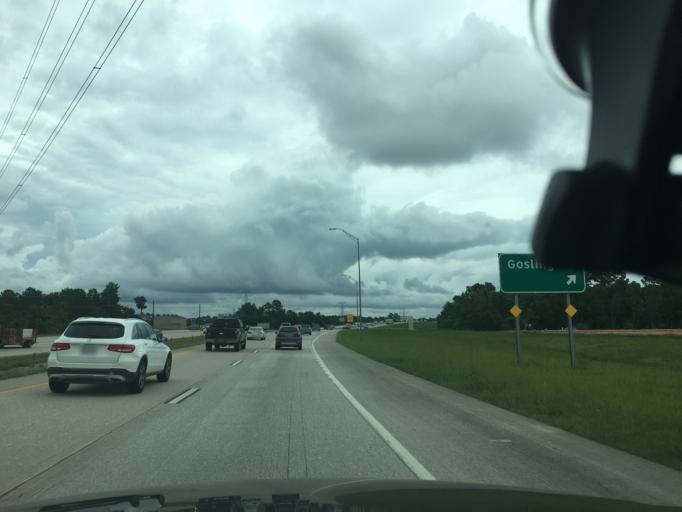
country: US
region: Texas
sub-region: Montgomery County
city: The Woodlands
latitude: 30.0933
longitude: -95.5137
